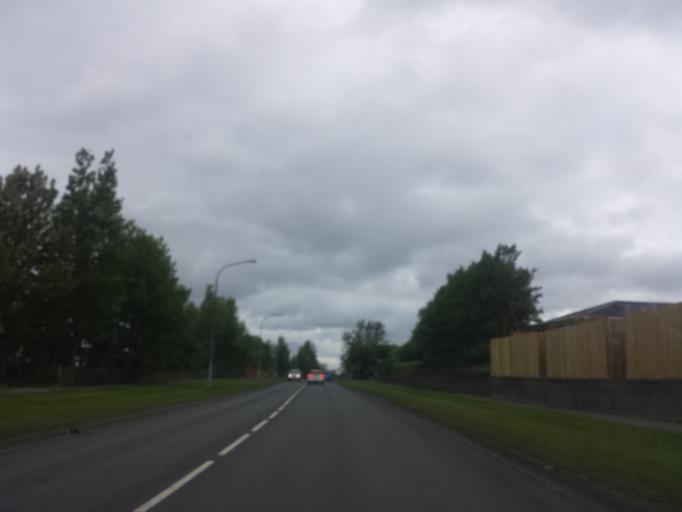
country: IS
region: Capital Region
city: Reykjavik
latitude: 64.1359
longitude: -21.8031
